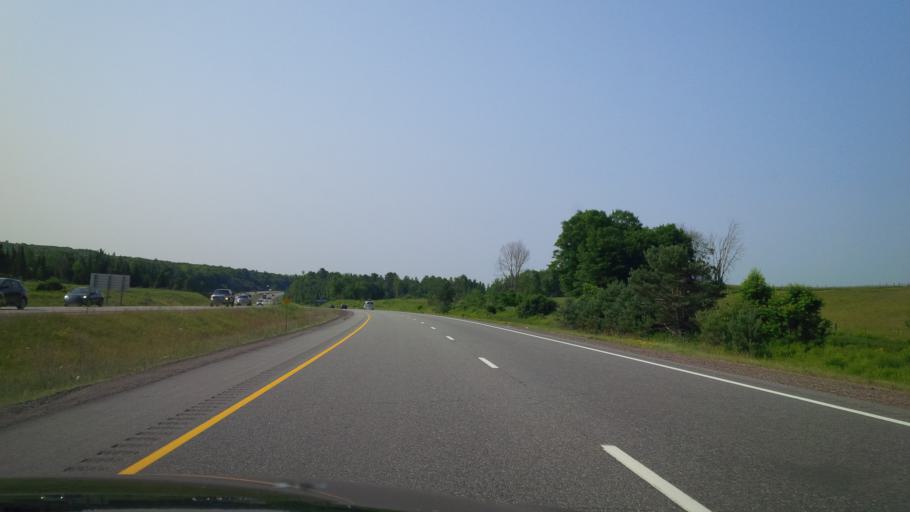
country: CA
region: Ontario
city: Bracebridge
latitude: 45.0342
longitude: -79.2930
